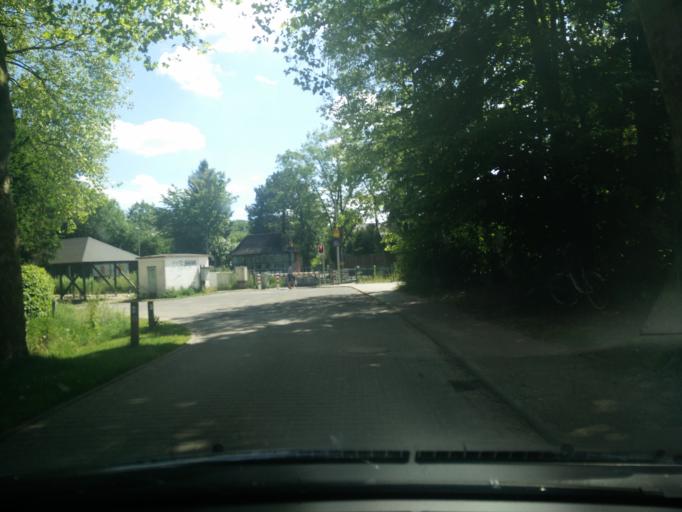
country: DE
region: Schleswig-Holstein
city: Prisdorf
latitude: 53.6758
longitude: 9.7603
